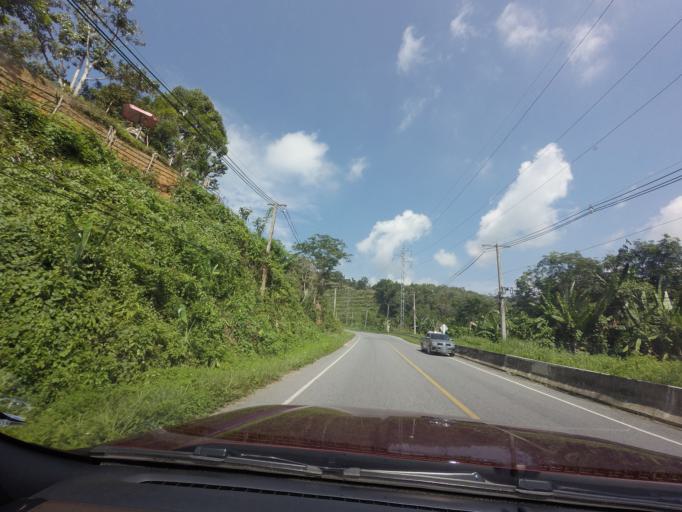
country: TH
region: Yala
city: Betong
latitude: 5.8798
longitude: 101.1367
